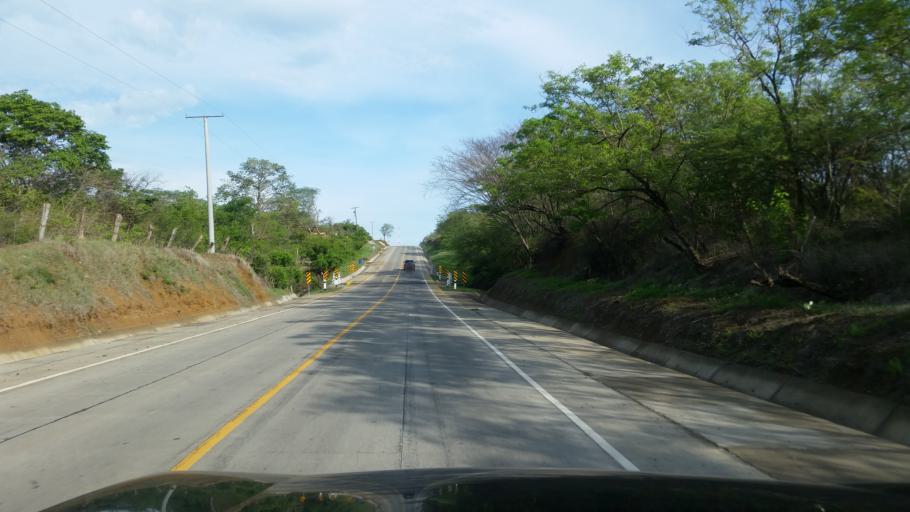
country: NI
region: Leon
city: Nagarote
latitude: 12.1140
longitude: -86.6081
